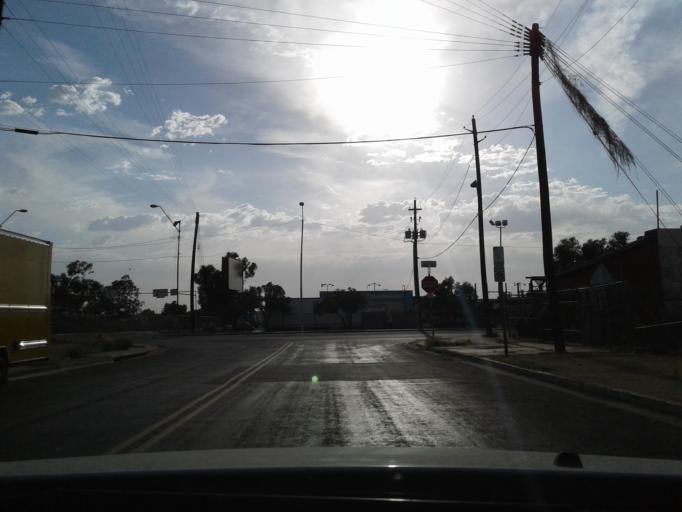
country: US
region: Arizona
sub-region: Maricopa County
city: Tempe Junction
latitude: 33.4463
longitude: -111.9949
